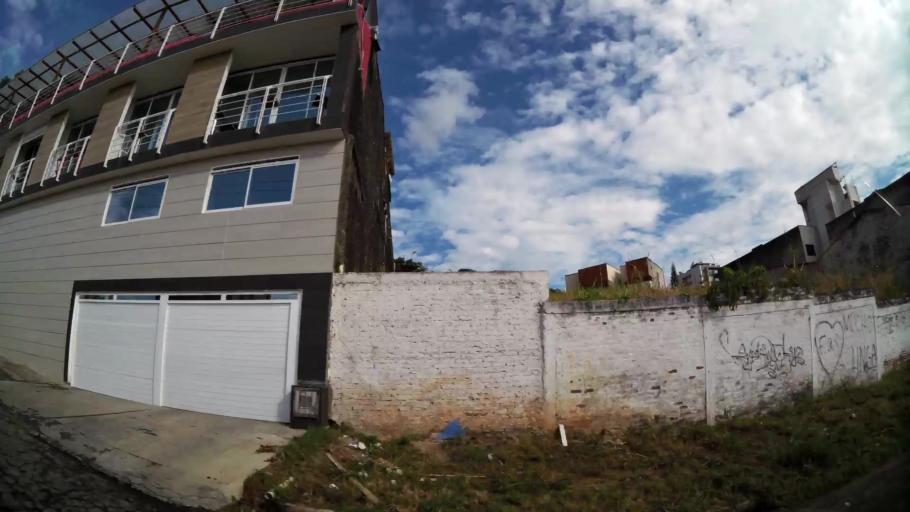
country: CO
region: Valle del Cauca
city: Cali
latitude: 3.4624
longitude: -76.5349
